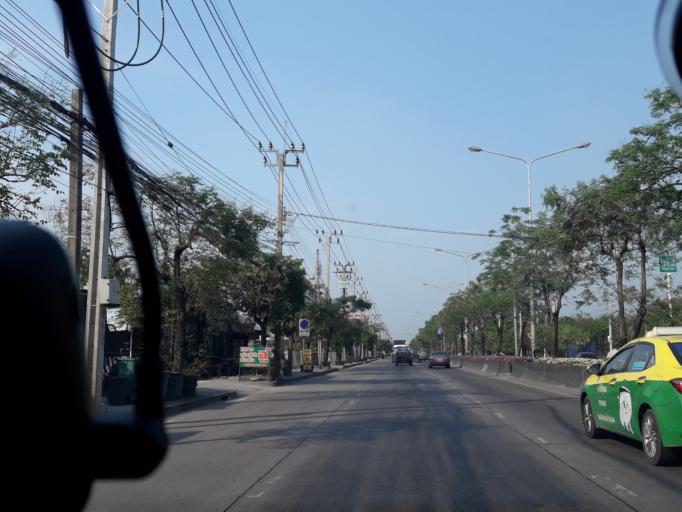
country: TH
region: Bangkok
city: Khlong Sam Wa
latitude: 13.8729
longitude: 100.7317
